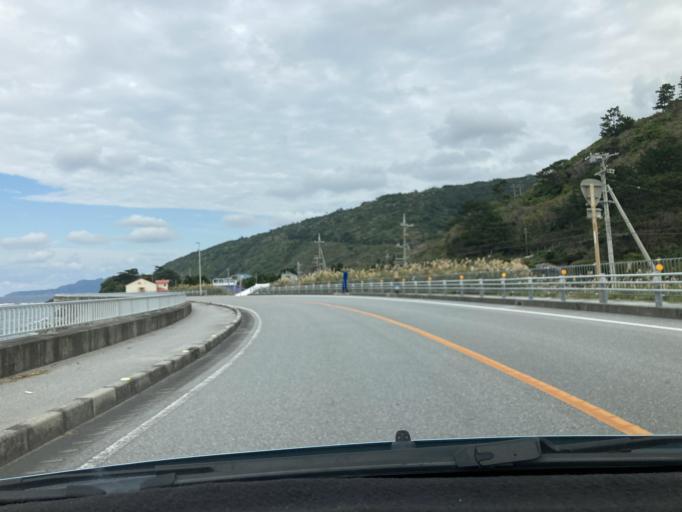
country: JP
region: Okinawa
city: Nago
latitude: 26.7840
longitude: 128.2186
